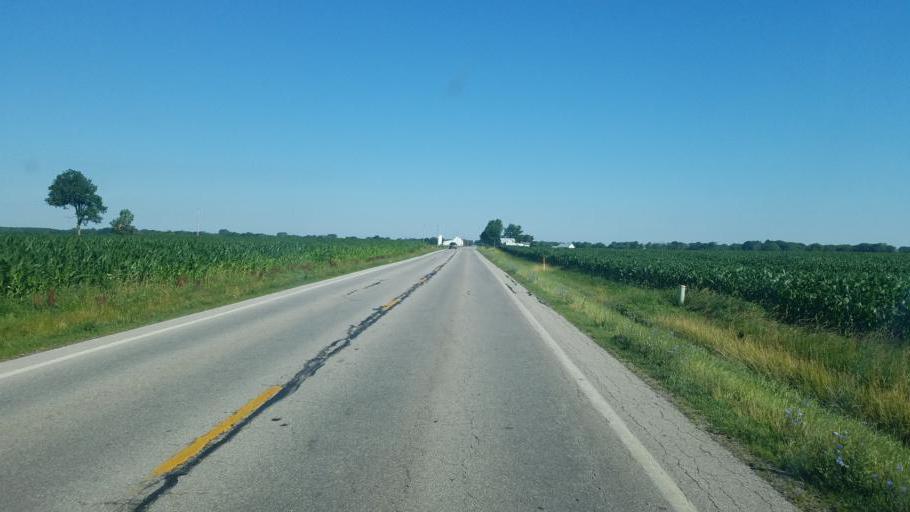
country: US
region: Ohio
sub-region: Morrow County
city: Mount Gilead
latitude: 40.5686
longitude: -82.8835
